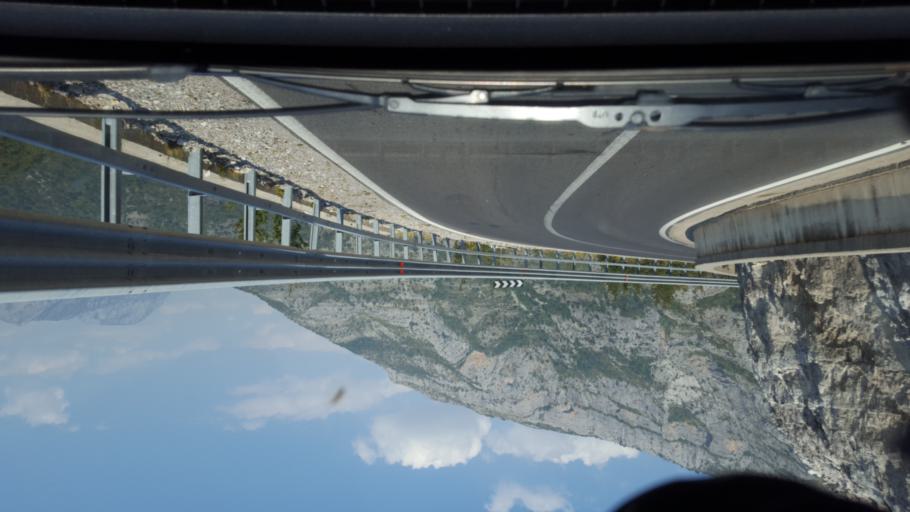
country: AL
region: Shkoder
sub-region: Rrethi i Malesia e Madhe
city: Kastrat
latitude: 42.4202
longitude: 19.5047
